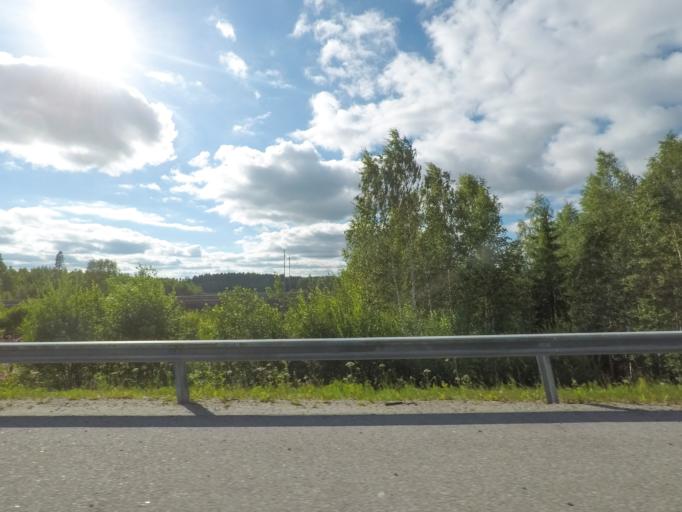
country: FI
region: Uusimaa
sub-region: Porvoo
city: Pukkila
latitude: 60.7680
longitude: 25.4685
